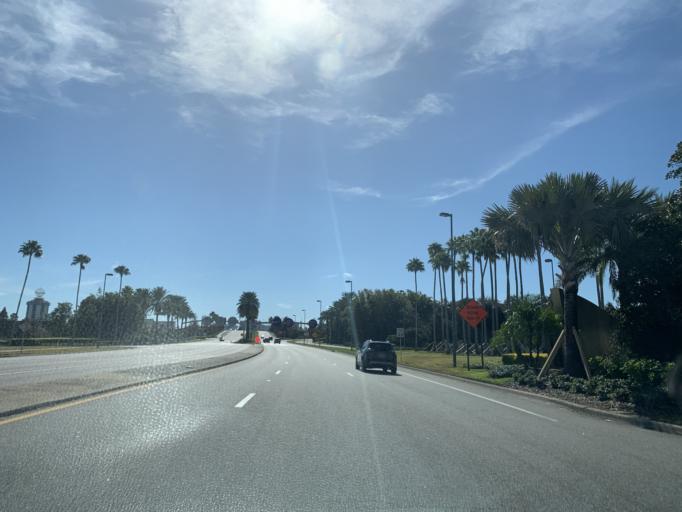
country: US
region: Florida
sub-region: Orange County
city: Tangelo Park
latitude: 28.4715
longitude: -81.4649
